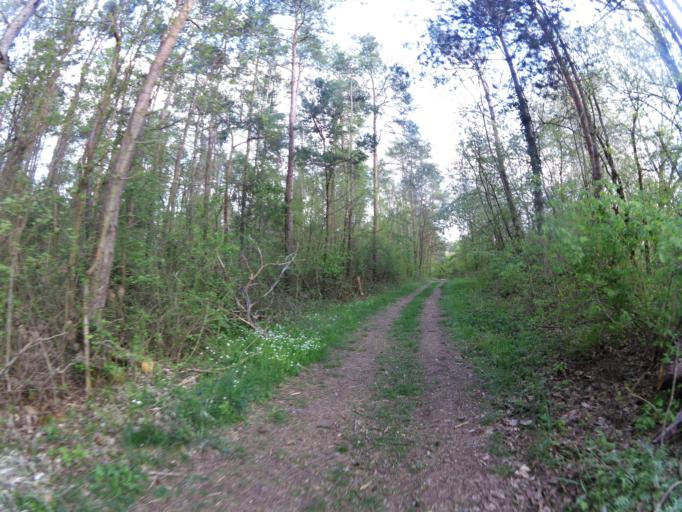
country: DE
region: Bavaria
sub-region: Regierungsbezirk Unterfranken
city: Winterhausen
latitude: 49.6976
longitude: 10.0096
